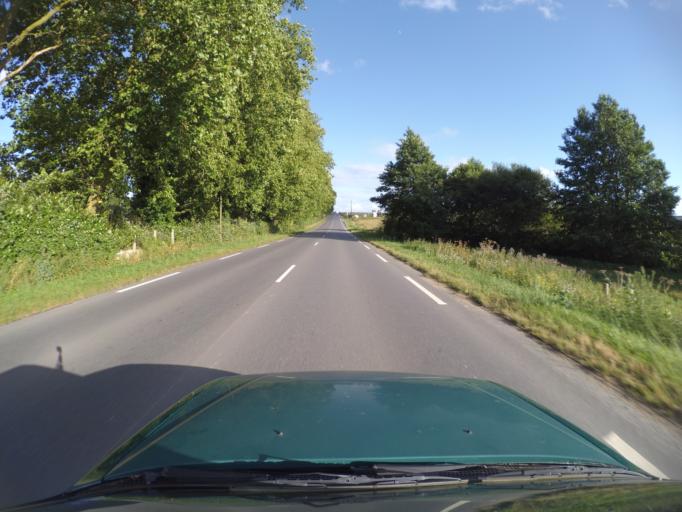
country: FR
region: Pays de la Loire
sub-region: Departement de la Loire-Atlantique
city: Remouille
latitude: 47.0493
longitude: -1.3657
